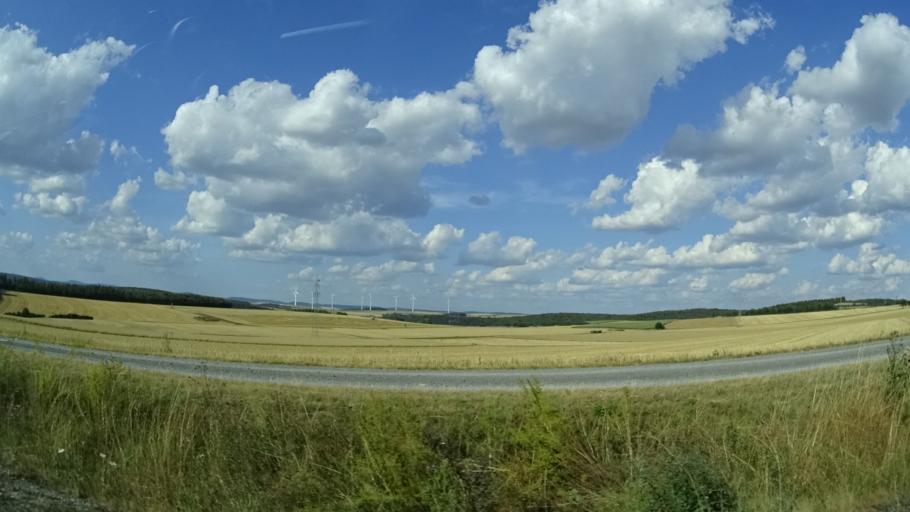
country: DE
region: Bavaria
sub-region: Regierungsbezirk Unterfranken
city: Heustreu
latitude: 50.3317
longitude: 10.2594
